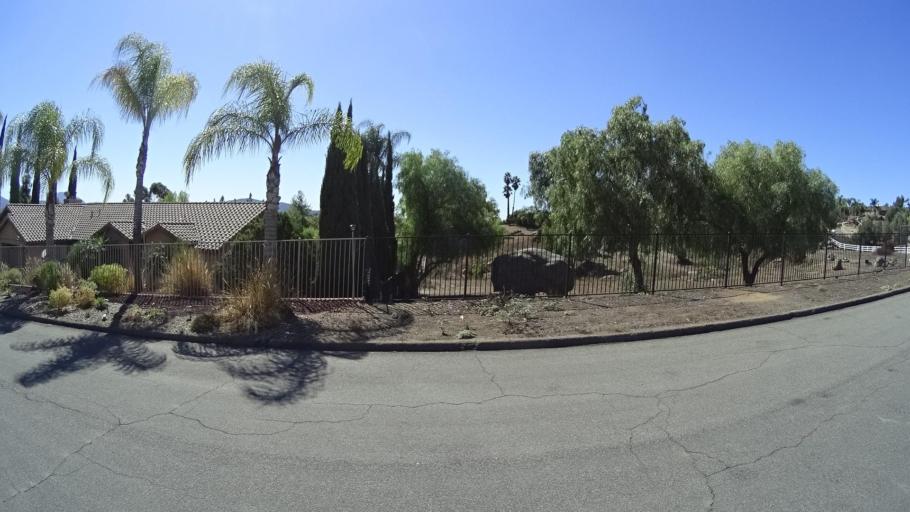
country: US
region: California
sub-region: San Diego County
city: Alpine
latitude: 32.8138
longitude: -116.7834
